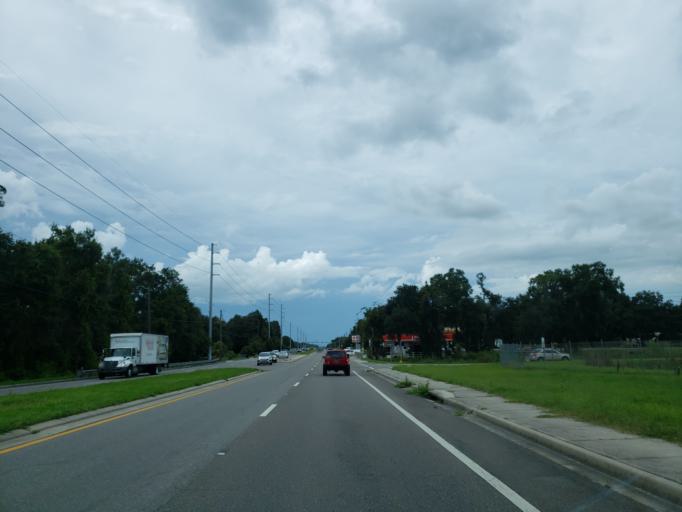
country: US
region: Florida
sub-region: Polk County
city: Willow Oak
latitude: 27.9481
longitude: -82.0553
